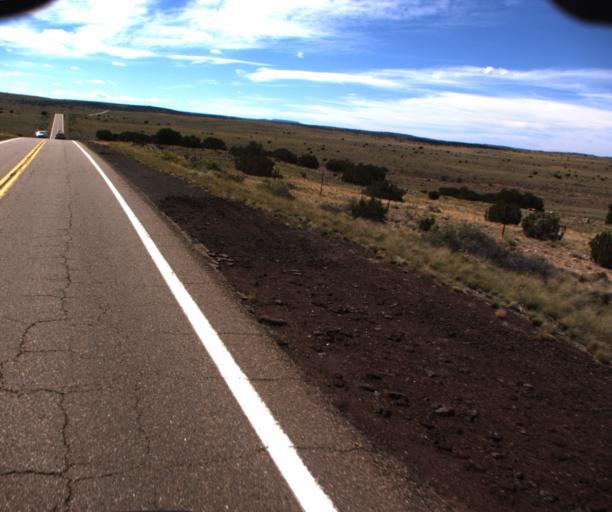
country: US
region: Arizona
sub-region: Apache County
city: Saint Johns
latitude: 34.4986
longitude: -109.5037
